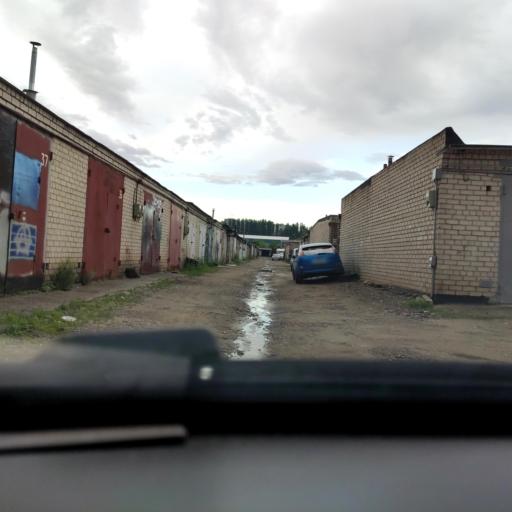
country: RU
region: Voronezj
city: Podgornoye
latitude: 51.7017
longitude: 39.1262
